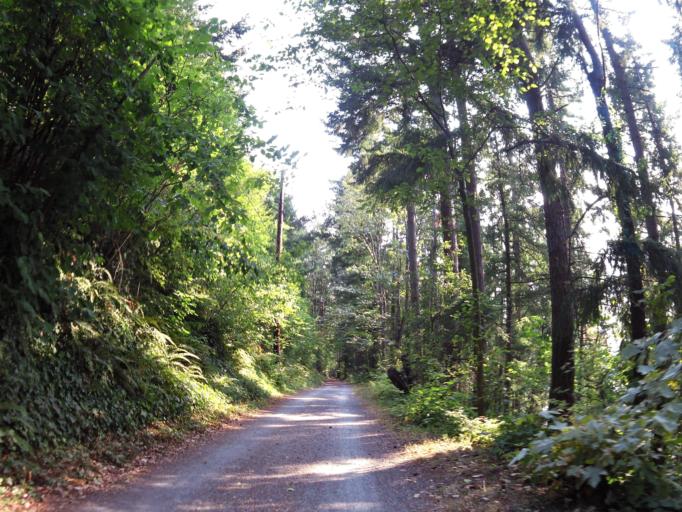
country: US
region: Washington
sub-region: Whatcom County
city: Bellingham
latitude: 48.6848
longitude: -122.4897
